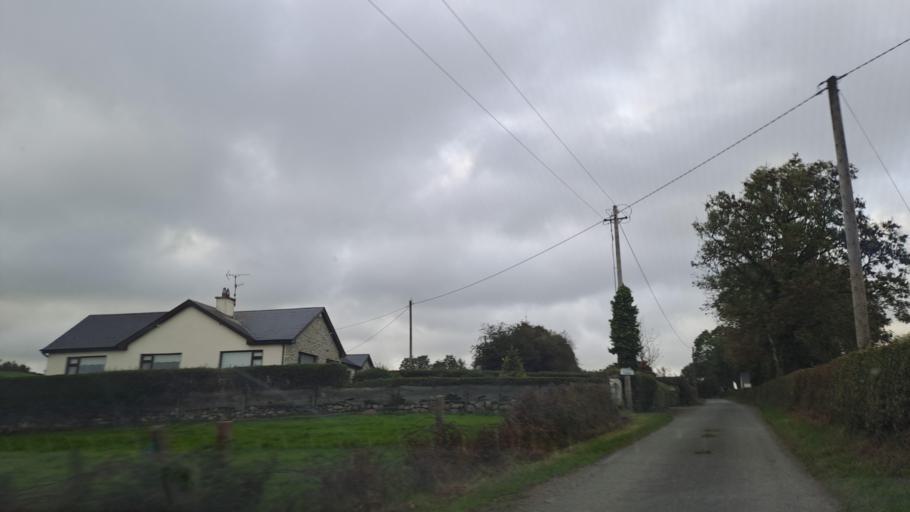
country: IE
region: Ulster
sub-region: County Monaghan
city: Carrickmacross
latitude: 54.0093
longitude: -6.7475
